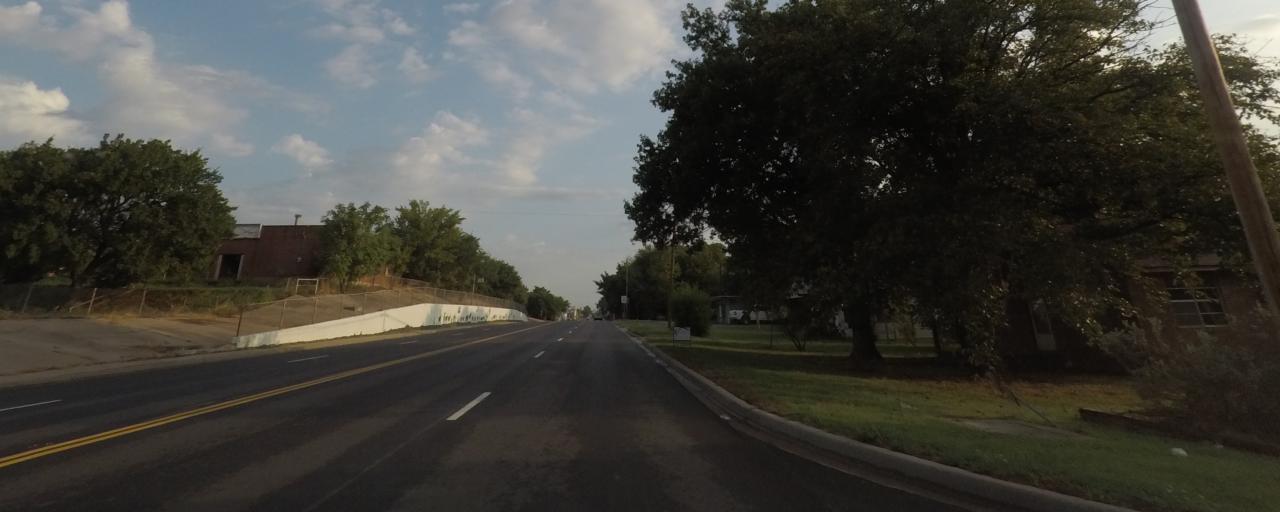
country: US
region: Oklahoma
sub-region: Stephens County
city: Comanche
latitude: 34.3637
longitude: -97.9642
